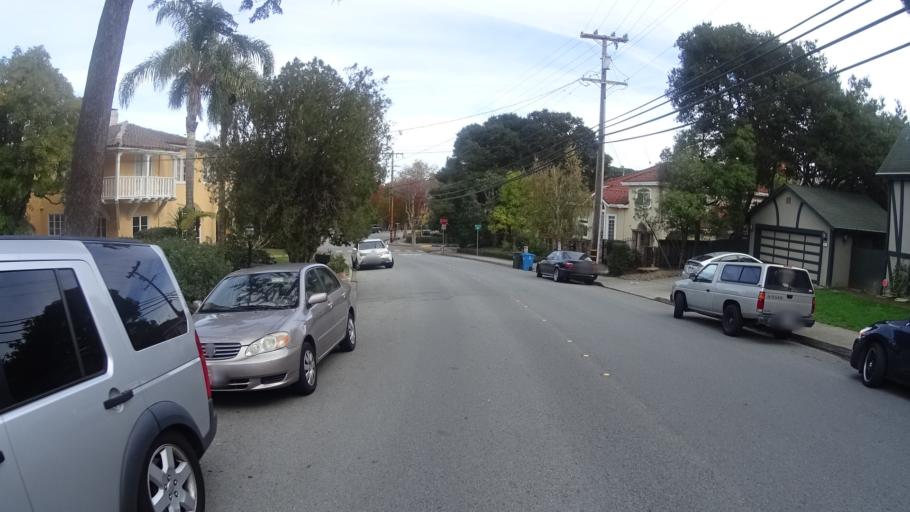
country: US
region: California
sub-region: San Mateo County
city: Hillsborough
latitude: 37.5787
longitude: -122.3814
